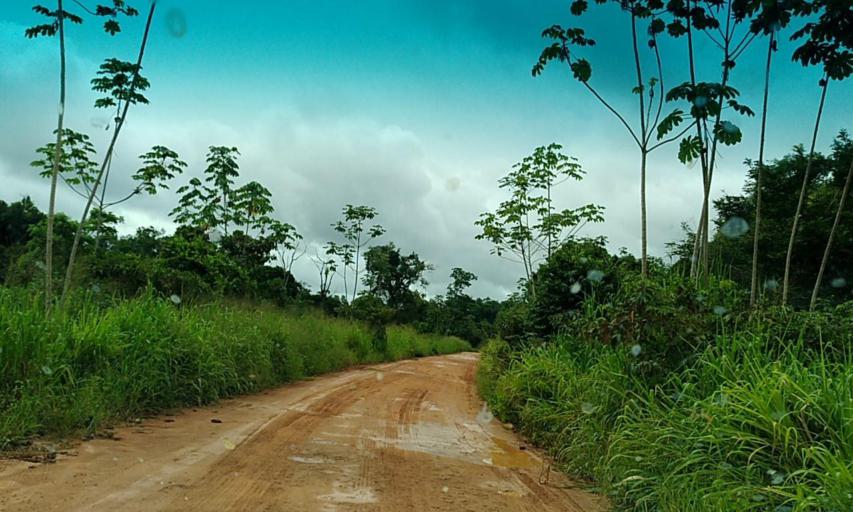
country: BR
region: Para
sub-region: Altamira
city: Altamira
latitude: -3.0834
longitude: -51.7011
